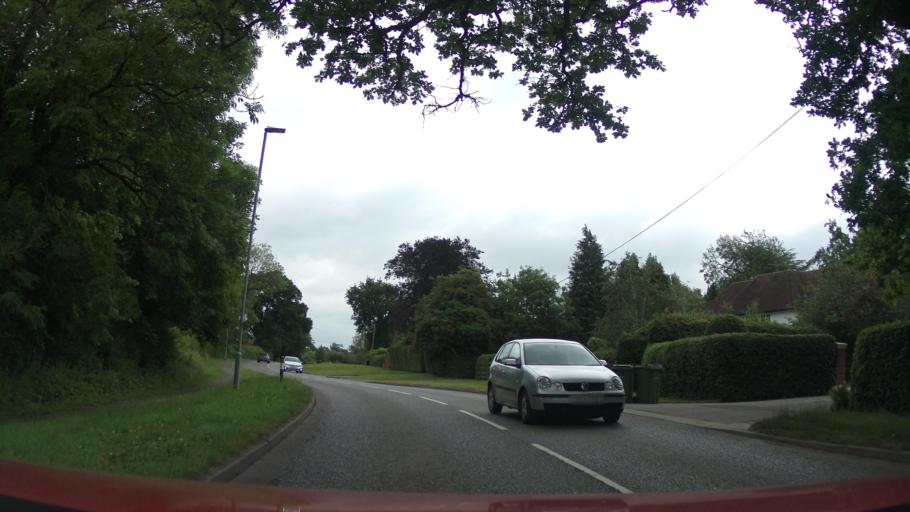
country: GB
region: England
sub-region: Leicestershire
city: Oadby
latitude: 52.6150
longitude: -1.0862
